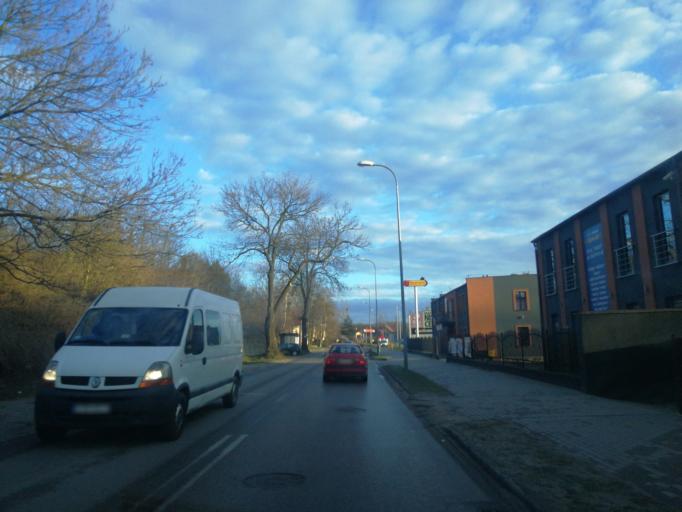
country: PL
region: Kujawsko-Pomorskie
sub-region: Powiat torunski
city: Chelmza
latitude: 53.1926
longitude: 18.6129
